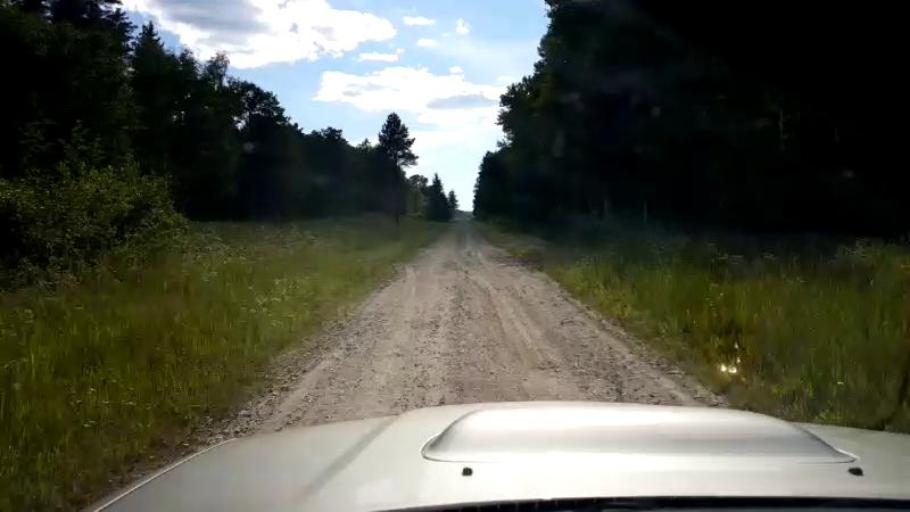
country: EE
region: Paernumaa
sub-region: Sindi linn
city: Sindi
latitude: 58.4934
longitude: 24.6120
